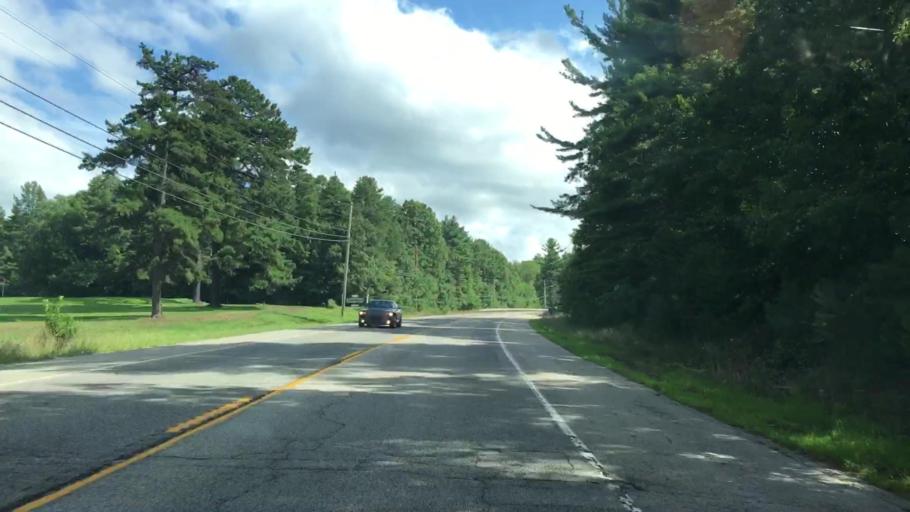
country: US
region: Maine
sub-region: York County
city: South Sanford
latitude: 43.3728
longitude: -70.7359
